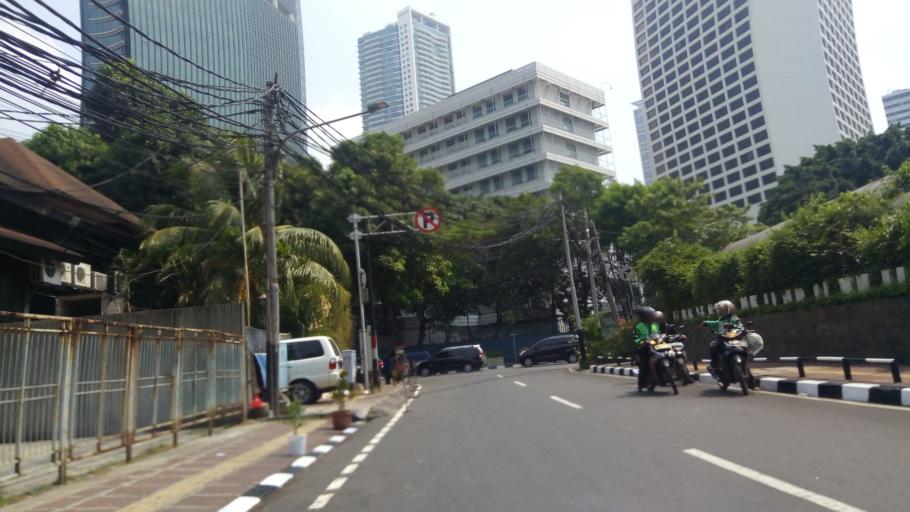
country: ID
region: Jakarta Raya
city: Jakarta
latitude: -6.1975
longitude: 106.8240
